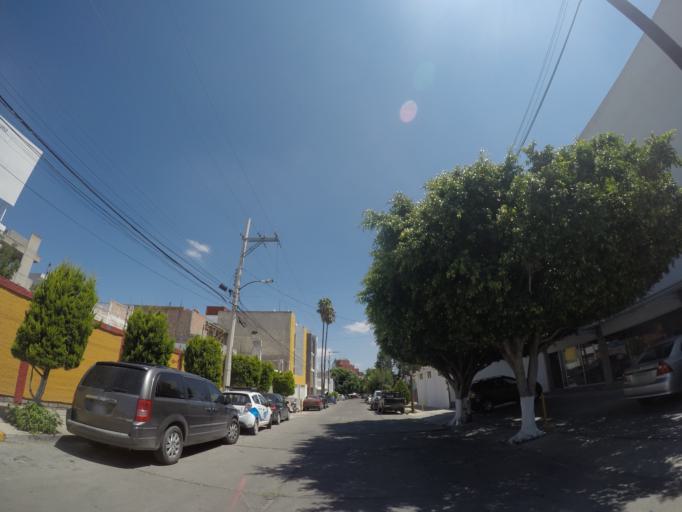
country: MX
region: San Luis Potosi
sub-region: San Luis Potosi
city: San Luis Potosi
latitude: 22.1463
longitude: -101.0087
